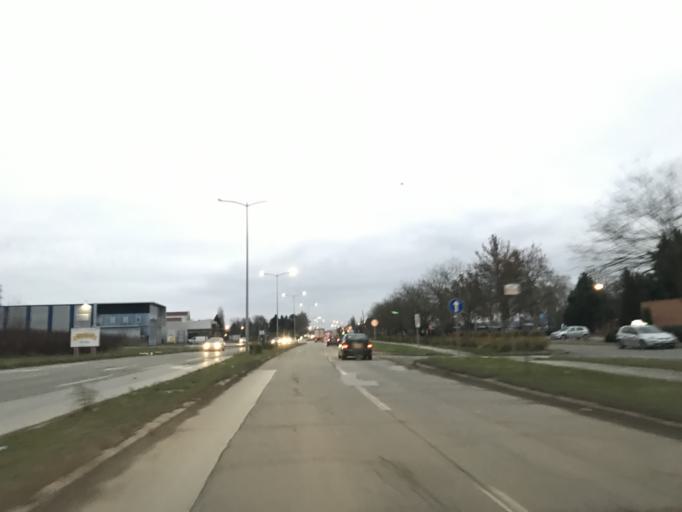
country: RS
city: Veternik
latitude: 45.2784
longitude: 19.7945
